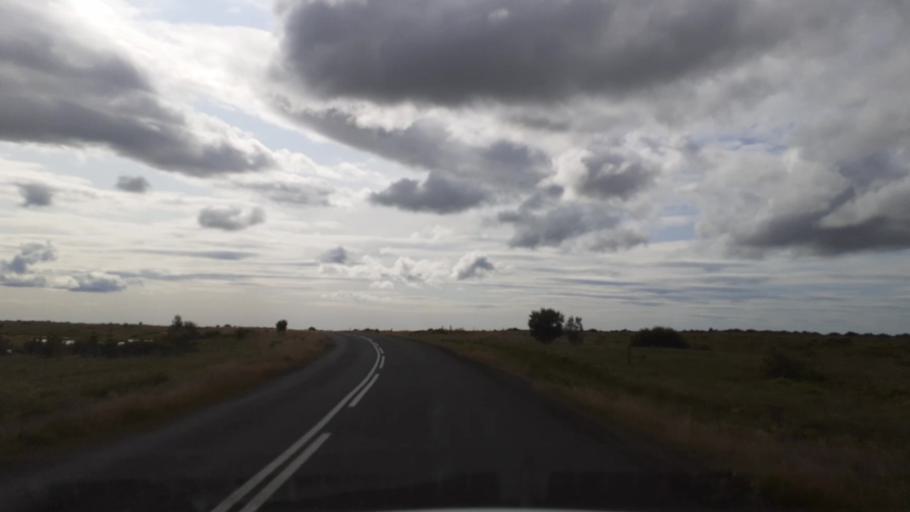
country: IS
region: South
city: Vestmannaeyjar
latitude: 63.8260
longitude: -20.4281
